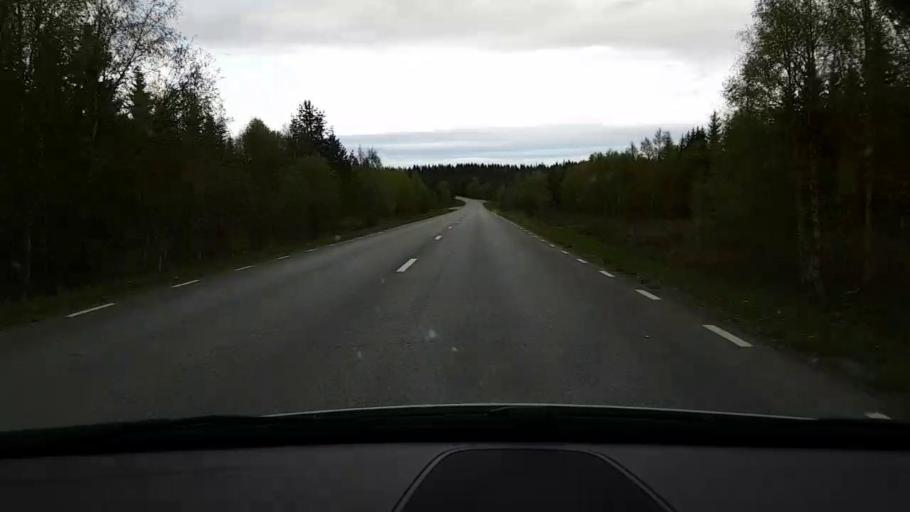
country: SE
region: Jaemtland
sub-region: Krokoms Kommun
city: Krokom
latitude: 63.0900
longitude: 14.2994
